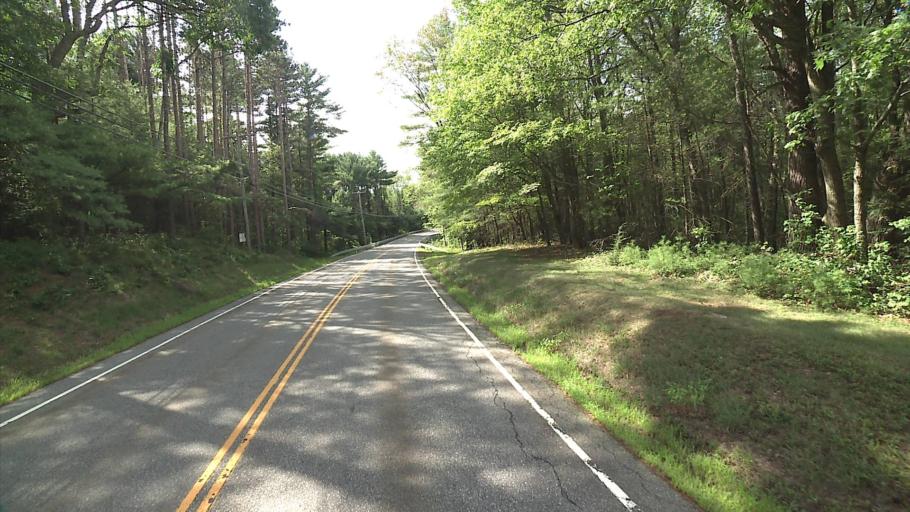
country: US
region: Massachusetts
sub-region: Hampden County
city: Holland
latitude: 42.0170
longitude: -72.1456
